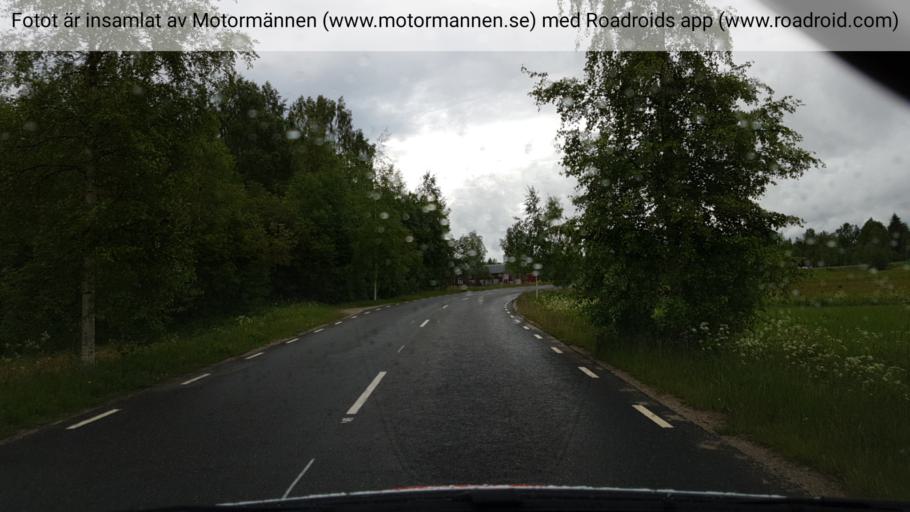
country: SE
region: Vaesterbotten
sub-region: Vannas Kommun
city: Vannasby
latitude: 63.8907
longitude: 19.8883
